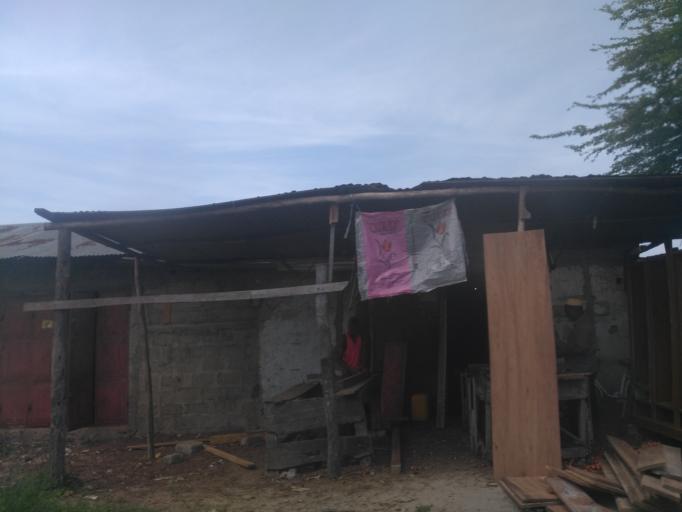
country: TZ
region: Zanzibar Urban/West
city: Zanzibar
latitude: -6.1519
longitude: 39.2095
